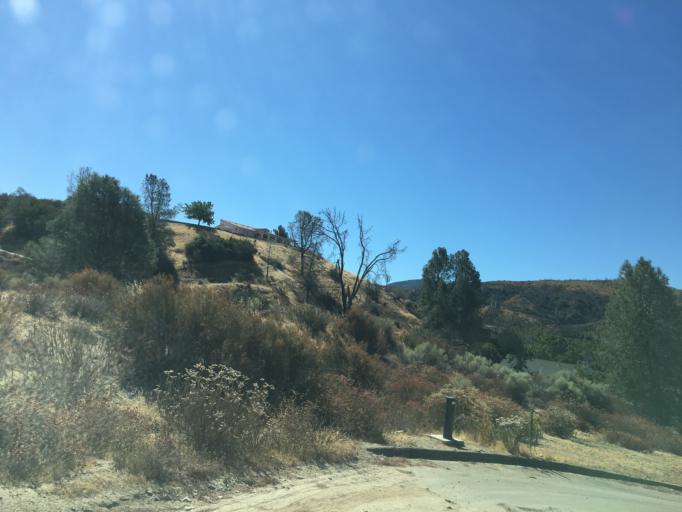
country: US
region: California
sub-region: Los Angeles County
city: Green Valley
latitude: 34.6764
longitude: -118.4393
